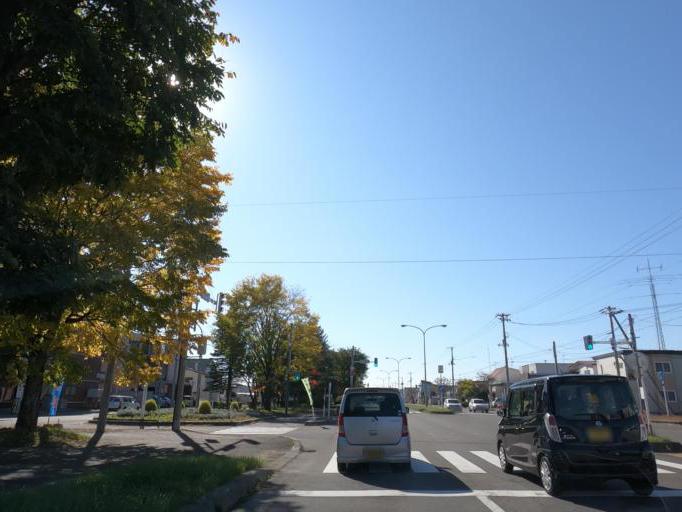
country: JP
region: Hokkaido
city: Obihiro
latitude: 42.9101
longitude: 143.2145
